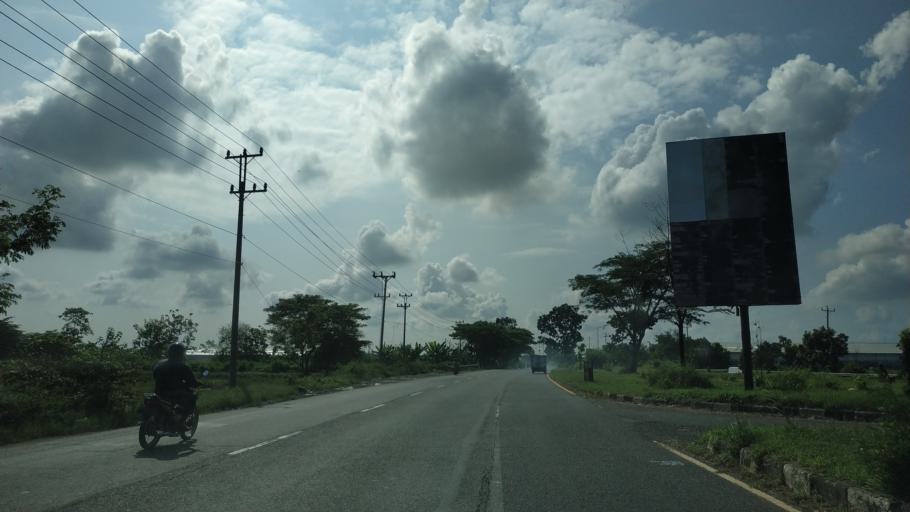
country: ID
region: Central Java
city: Comal
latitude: -6.9003
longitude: 109.5086
